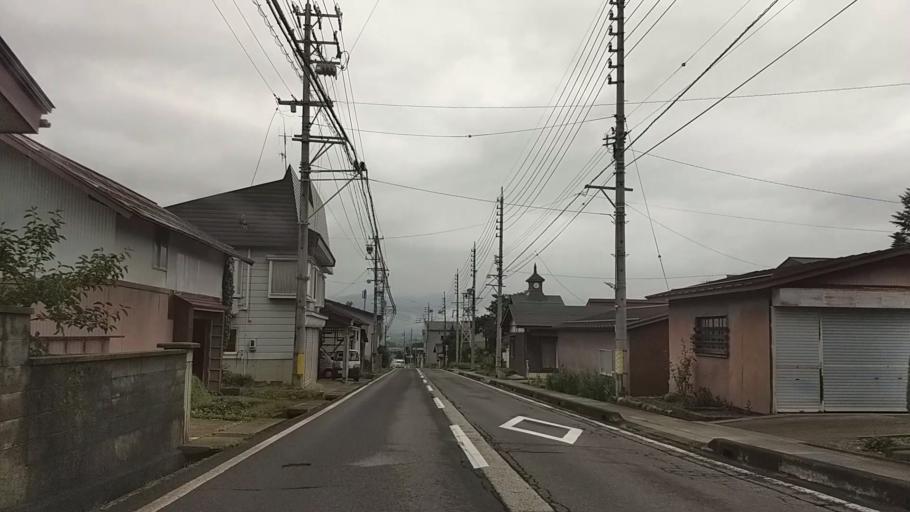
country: JP
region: Nagano
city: Iiyama
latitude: 36.8375
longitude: 138.4086
